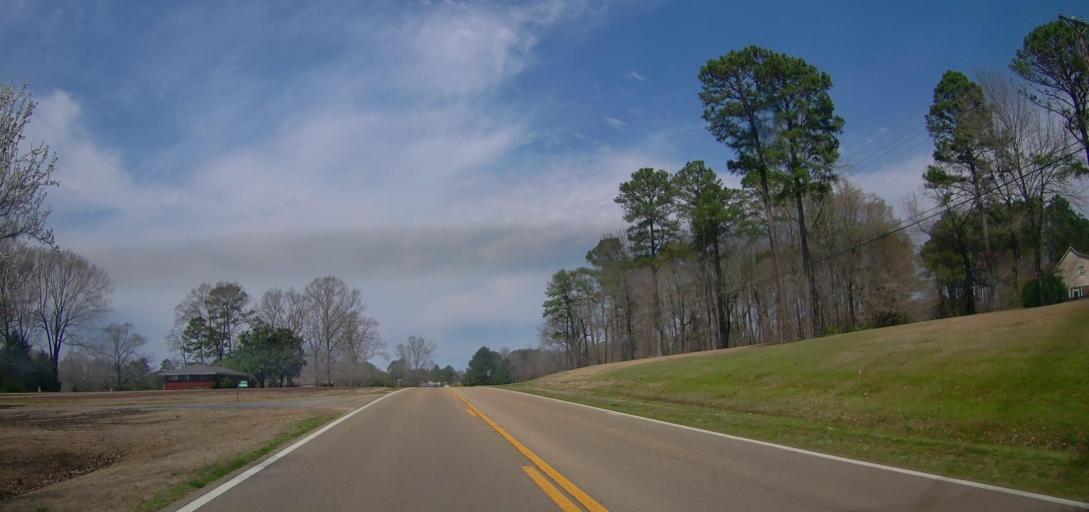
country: US
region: Mississippi
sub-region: Union County
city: New Albany
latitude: 34.4481
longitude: -88.9686
